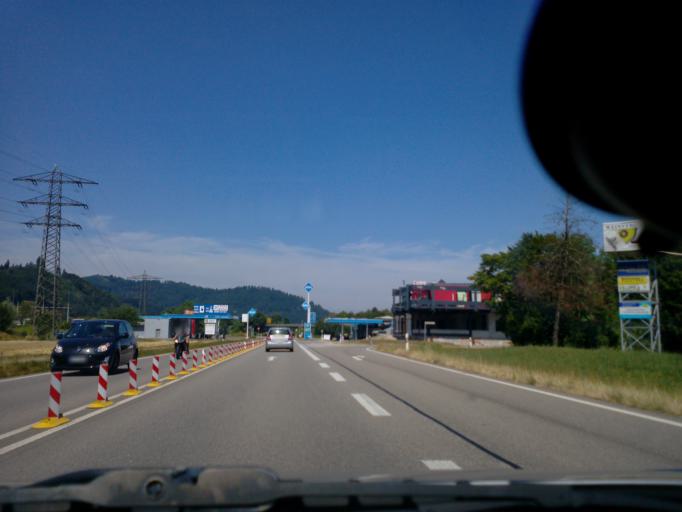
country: DE
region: Hesse
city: Gengenbach
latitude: 48.3988
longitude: 8.0096
